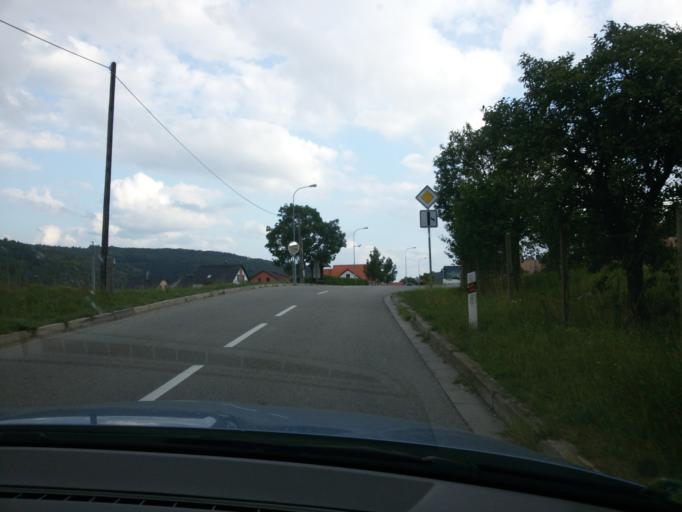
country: CZ
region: South Moravian
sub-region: Okres Brno-Venkov
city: Lomnice
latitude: 49.4108
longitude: 16.4079
